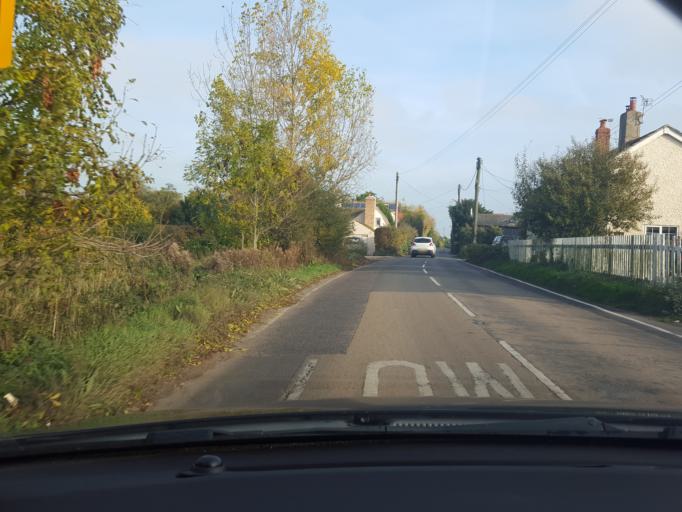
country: GB
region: England
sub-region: Essex
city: Frinton-on-Sea
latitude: 51.8545
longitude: 1.2152
